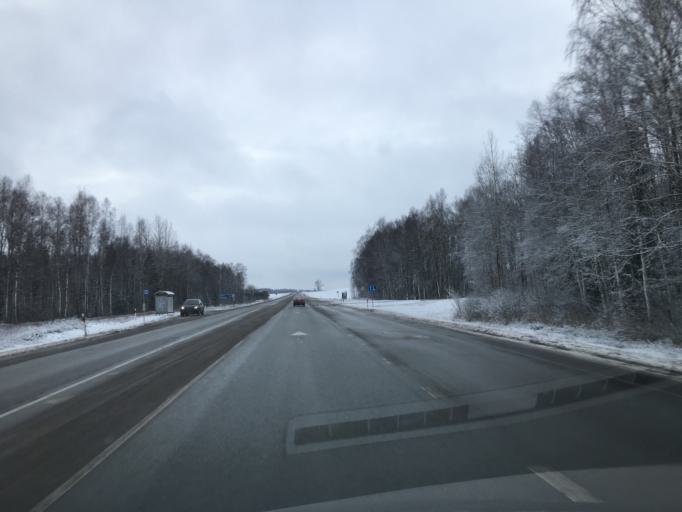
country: EE
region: Tartu
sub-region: Noo vald
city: Noo
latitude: 58.3073
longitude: 26.5978
